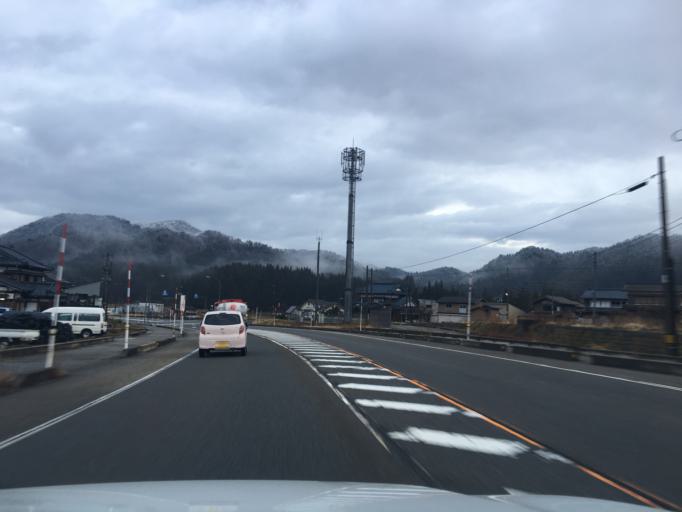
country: JP
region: Niigata
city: Murakami
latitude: 38.4386
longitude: 139.5917
